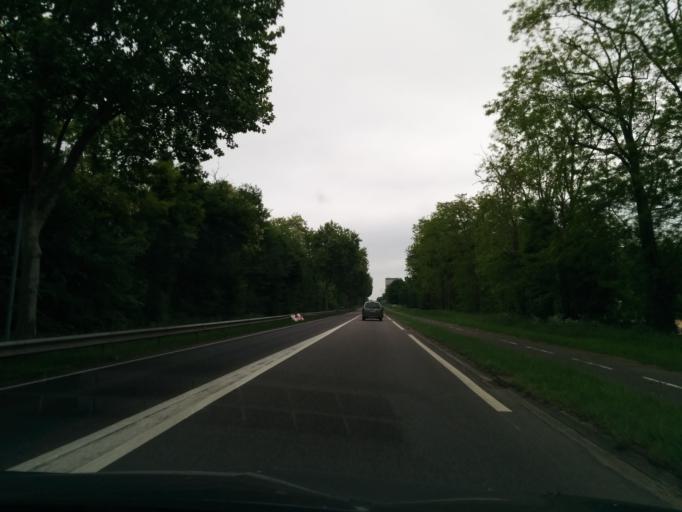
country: FR
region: Ile-de-France
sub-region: Departement des Yvelines
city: Buchelay
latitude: 48.9976
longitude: 1.6673
